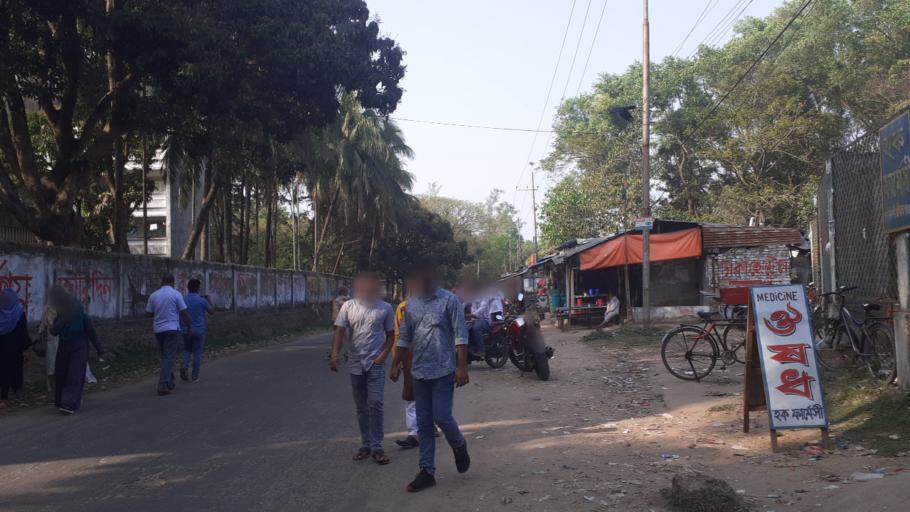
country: BD
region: Chittagong
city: Chittagong
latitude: 22.4731
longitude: 91.7933
